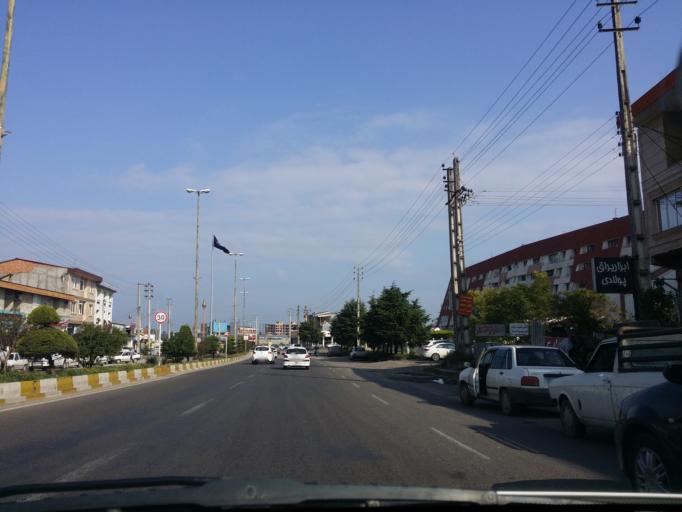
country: IR
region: Mazandaran
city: Chalus
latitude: 36.6800
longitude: 51.4028
